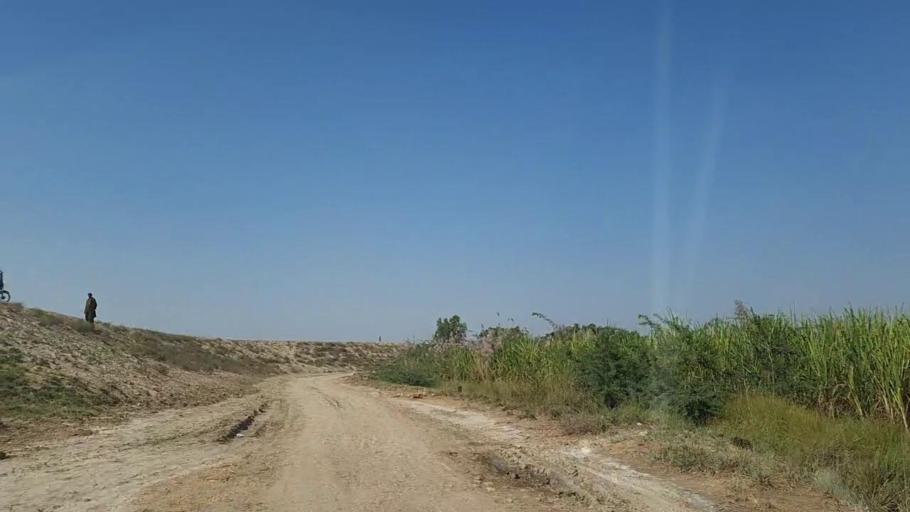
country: PK
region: Sindh
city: Chuhar Jamali
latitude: 24.5819
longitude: 68.0312
